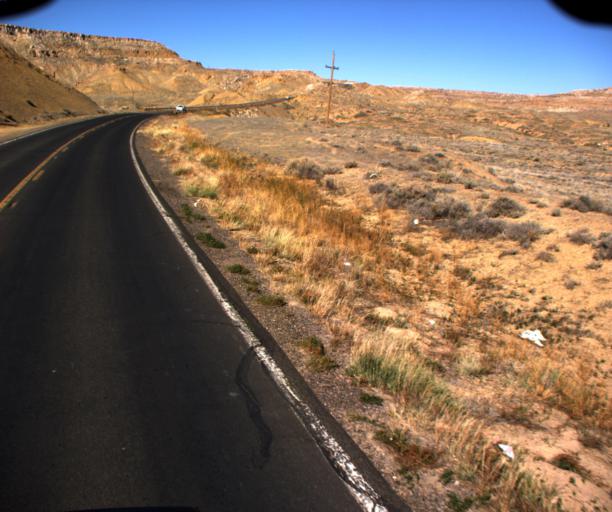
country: US
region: Arizona
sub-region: Navajo County
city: First Mesa
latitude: 35.7956
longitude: -110.5116
